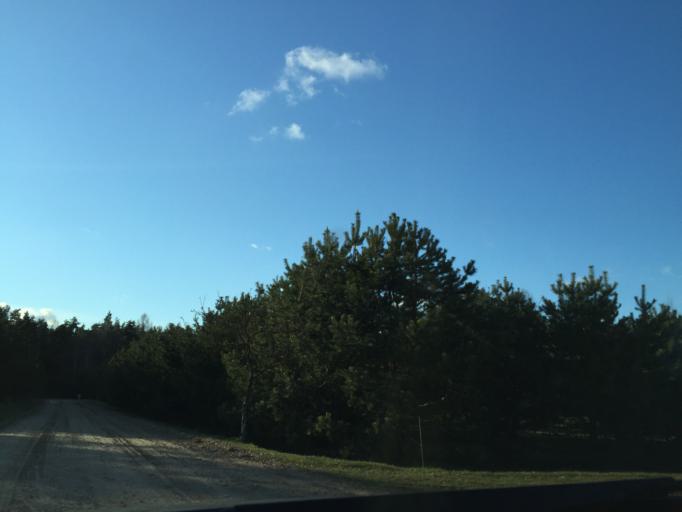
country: LV
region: Kekava
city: Kekava
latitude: 56.8530
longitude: 24.2348
